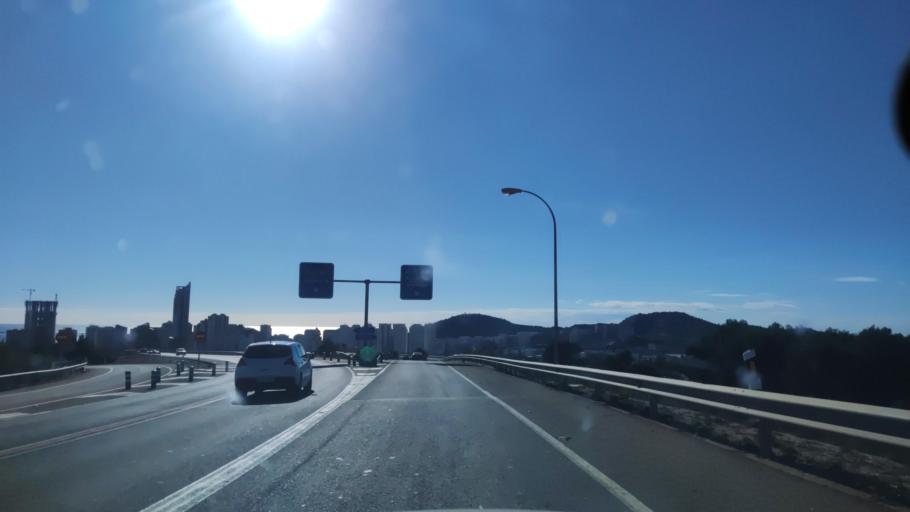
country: ES
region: Valencia
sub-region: Provincia de Alicante
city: Benidorm
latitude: 38.5460
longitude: -0.1720
